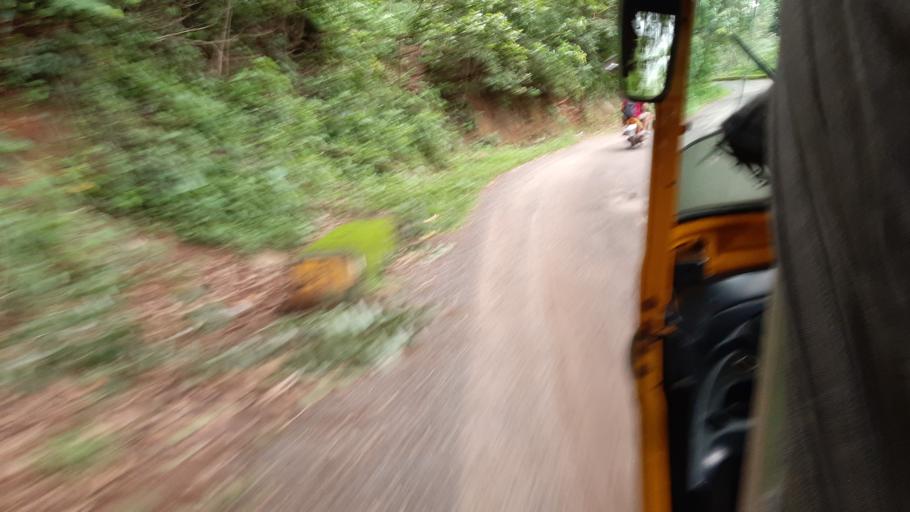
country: IN
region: Andhra Pradesh
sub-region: Vizianagaram District
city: Salur
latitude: 18.2419
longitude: 83.0170
